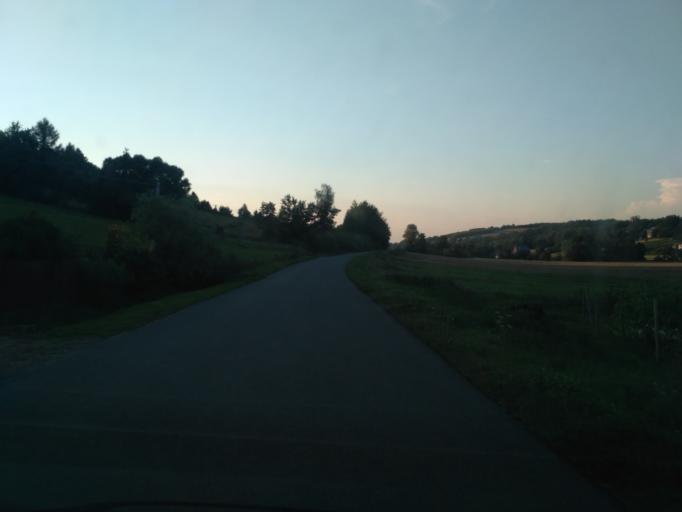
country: PL
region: Subcarpathian Voivodeship
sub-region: Powiat strzyzowski
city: Wysoka Strzyzowska
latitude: 49.7982
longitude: 21.7527
